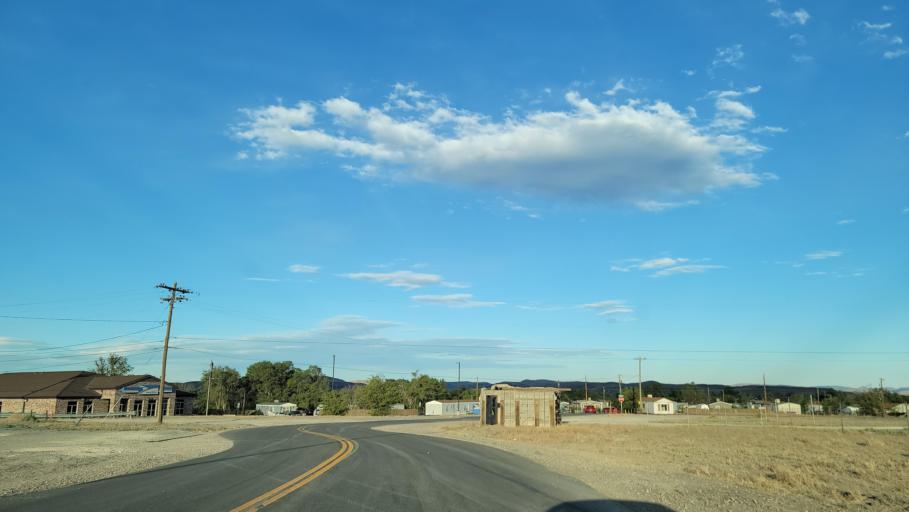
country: US
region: Nevada
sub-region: Lyon County
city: Silver Springs
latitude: 39.4147
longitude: -119.2250
